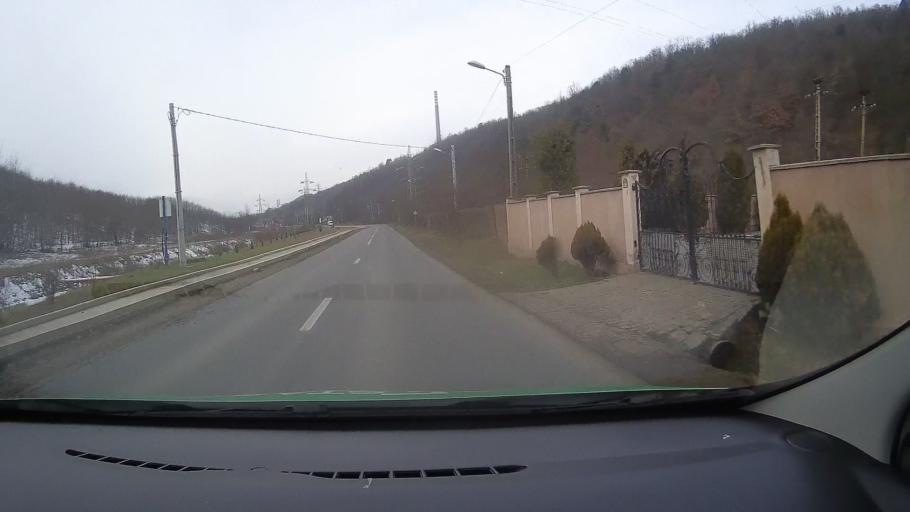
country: RO
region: Alba
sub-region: Oras Zlatna
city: Zlatna
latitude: 46.1034
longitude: 23.2462
